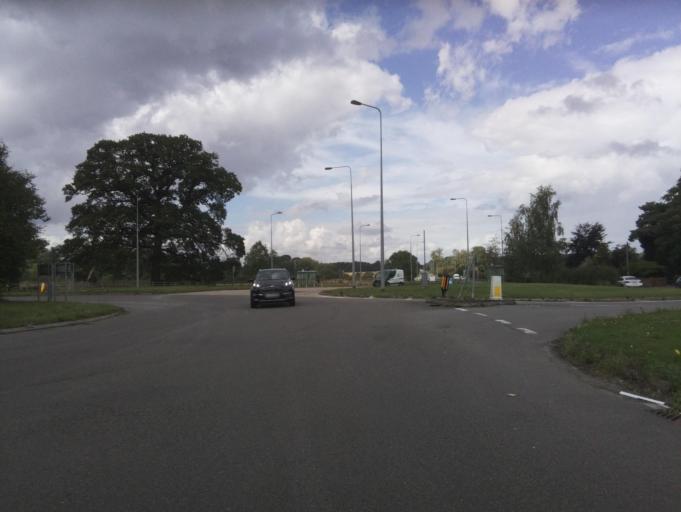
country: GB
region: England
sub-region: Staffordshire
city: Barlaston
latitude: 52.9481
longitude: -2.1908
